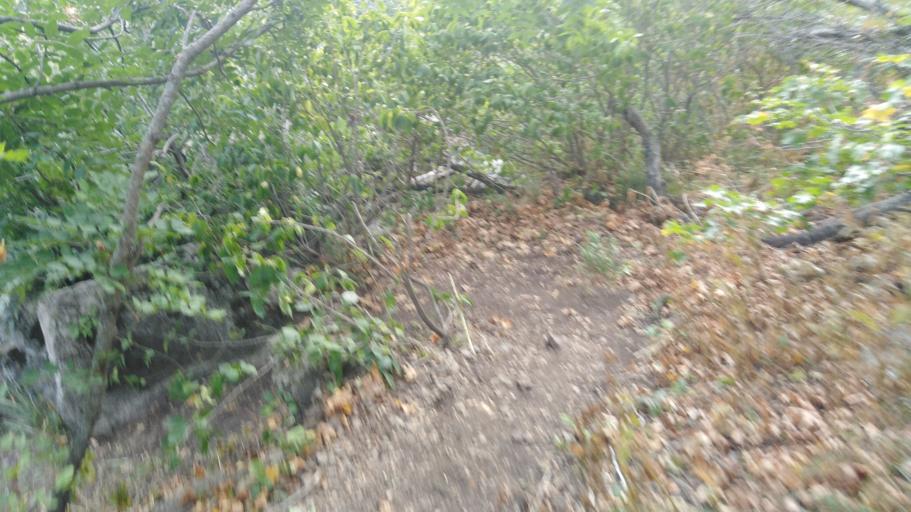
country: RU
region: Stavropol'skiy
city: Zheleznovodsk
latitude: 44.0968
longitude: 43.0274
